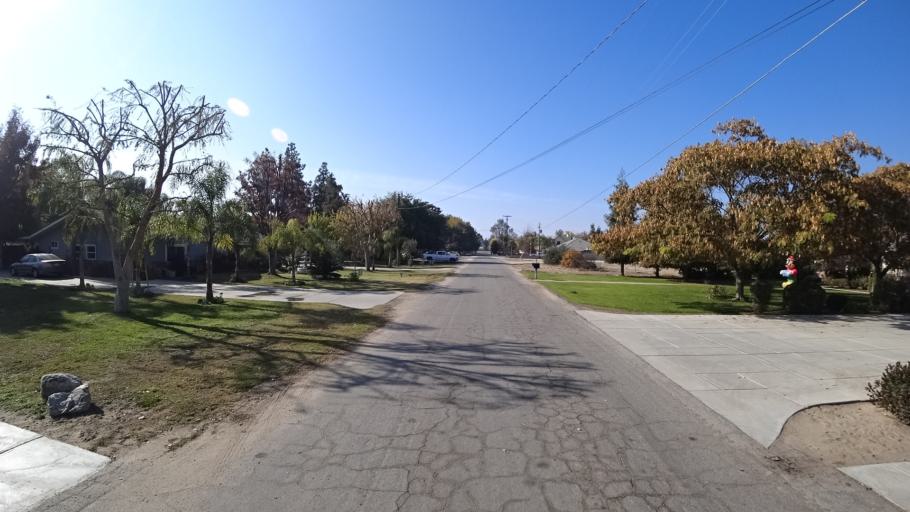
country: US
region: California
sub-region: Kern County
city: Rosedale
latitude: 35.3635
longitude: -119.1687
